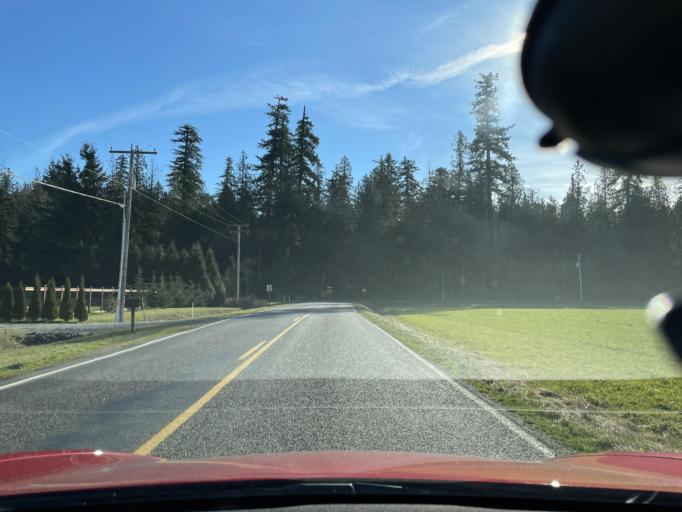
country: US
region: Washington
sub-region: Whatcom County
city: Lynden
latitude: 48.9658
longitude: -122.5129
